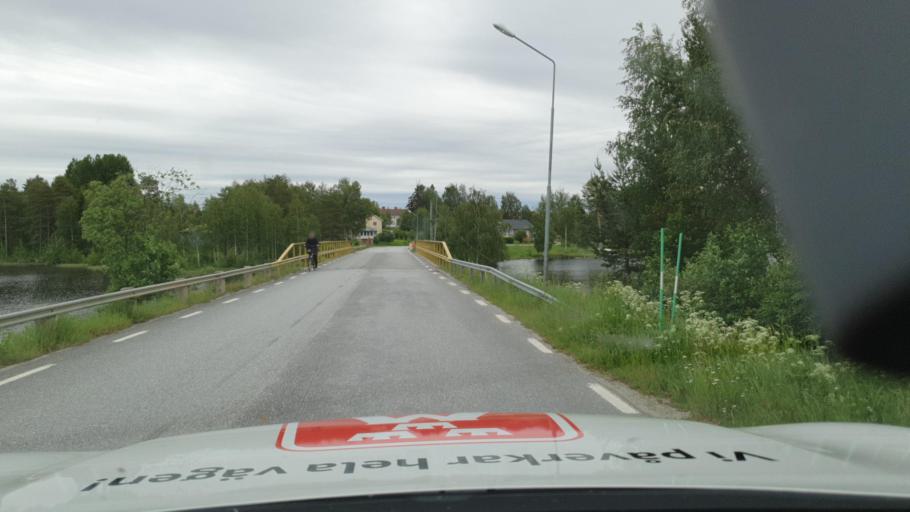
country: SE
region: Vaesterbotten
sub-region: Lycksele Kommun
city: Lycksele
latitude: 64.0808
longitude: 18.4001
